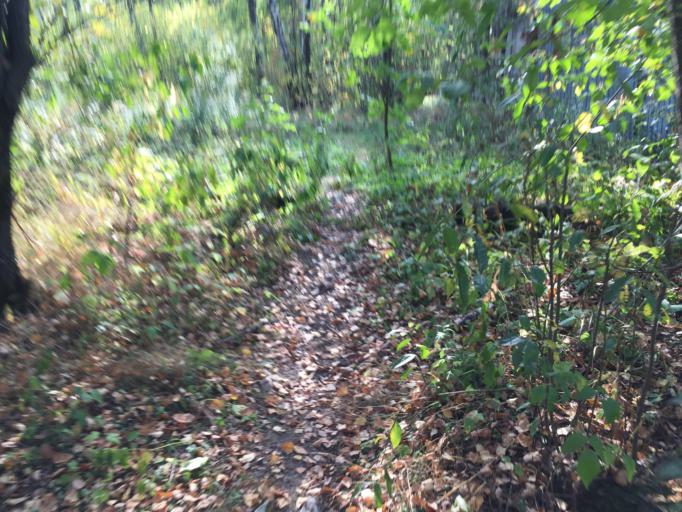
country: RU
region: Moscow
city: Babushkin
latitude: 55.8501
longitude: 37.7196
